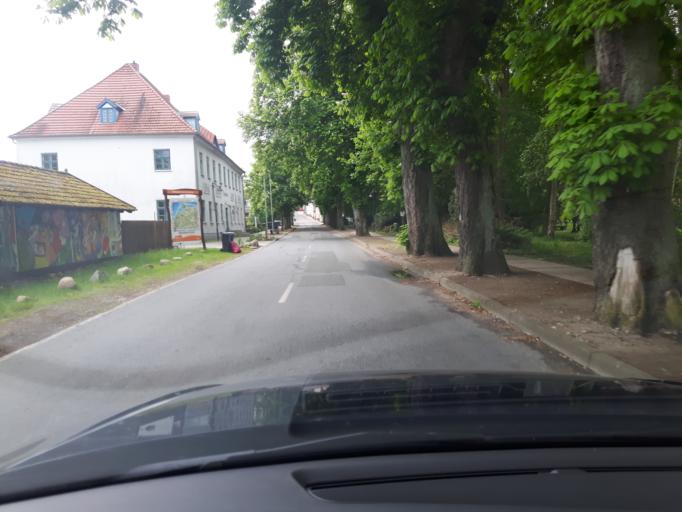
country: DE
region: Mecklenburg-Vorpommern
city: Bad Sulze
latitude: 54.1131
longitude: 12.6620
